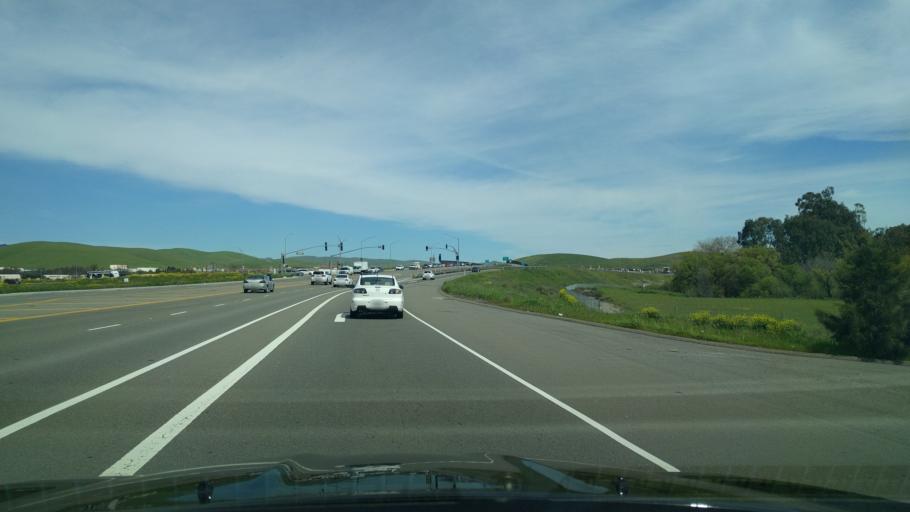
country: US
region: California
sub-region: Alameda County
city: Livermore
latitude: 37.6978
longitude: -121.8048
